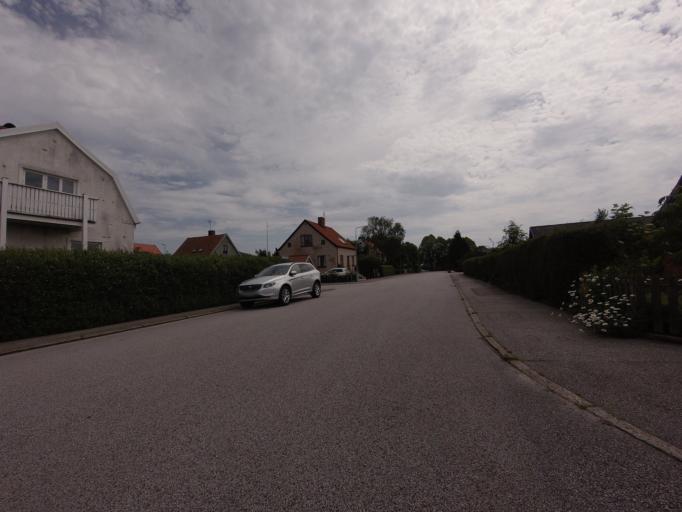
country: SE
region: Skane
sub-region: Ystads Kommun
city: Ystad
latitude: 55.4283
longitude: 13.8037
